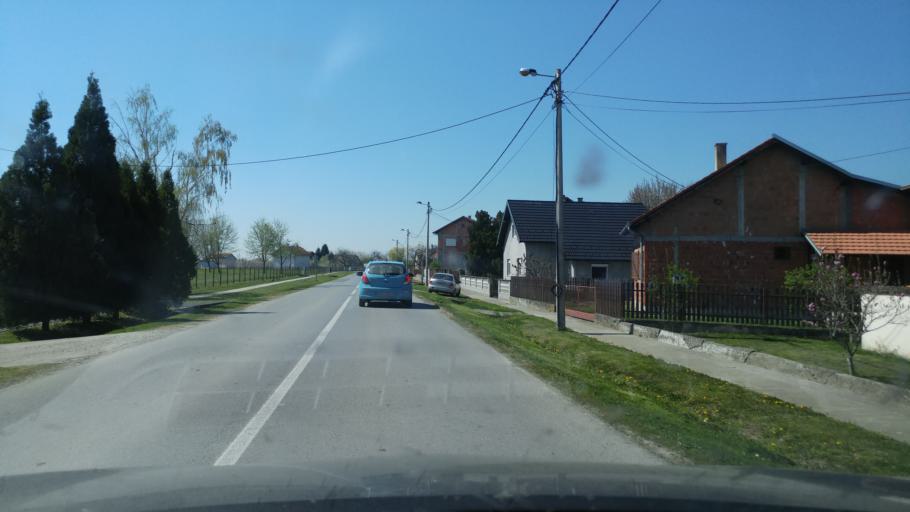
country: HR
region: Osjecko-Baranjska
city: Laslovo
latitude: 45.4120
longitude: 18.7093
